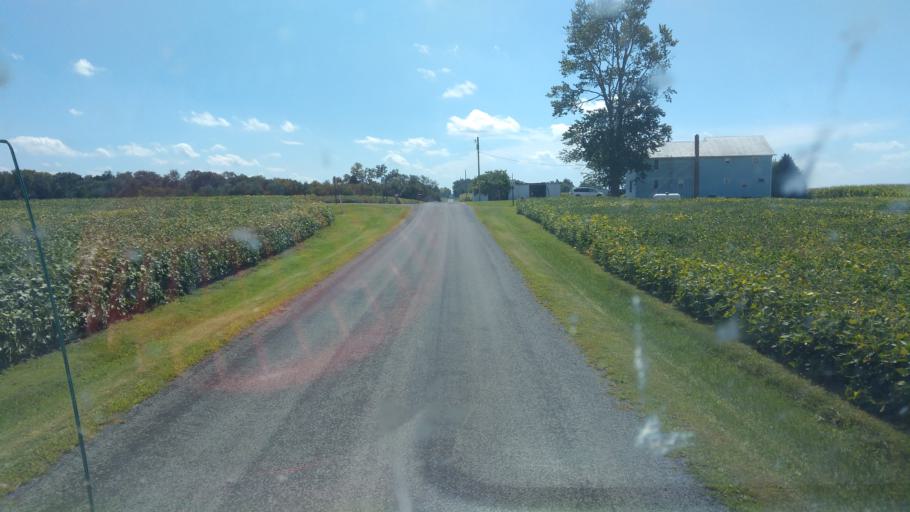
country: US
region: Ohio
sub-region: Marion County
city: Marion
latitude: 40.7029
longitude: -83.1688
